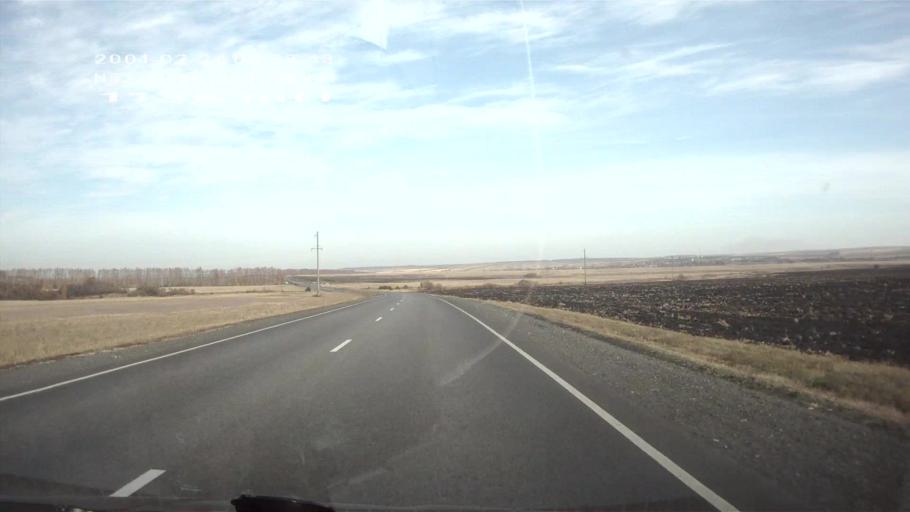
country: RU
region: Penza
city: Mokshan
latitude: 53.5750
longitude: 44.7289
